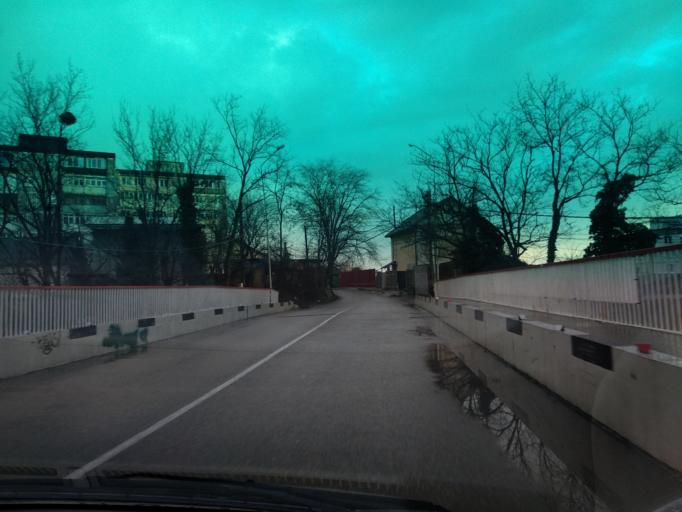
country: RU
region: Krasnodarskiy
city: Tuapse
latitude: 44.1071
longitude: 39.0808
